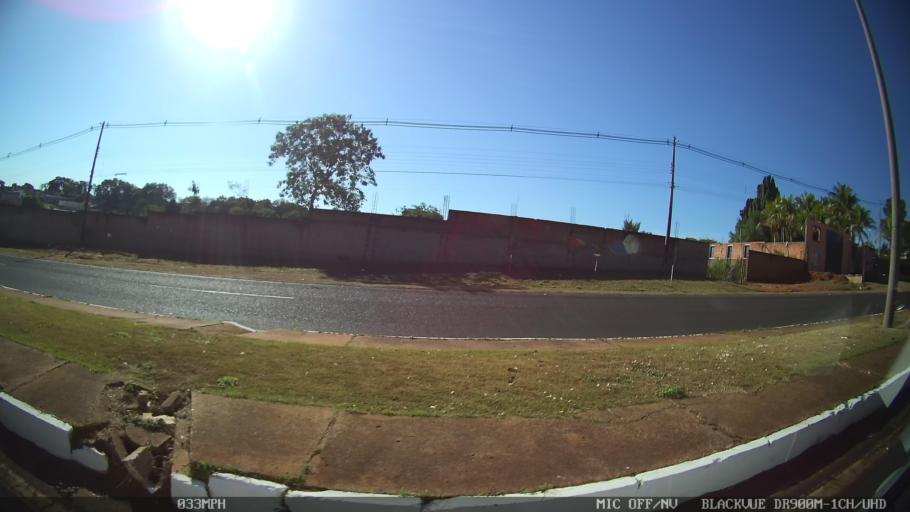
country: BR
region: Sao Paulo
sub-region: Olimpia
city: Olimpia
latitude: -20.7387
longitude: -48.9006
